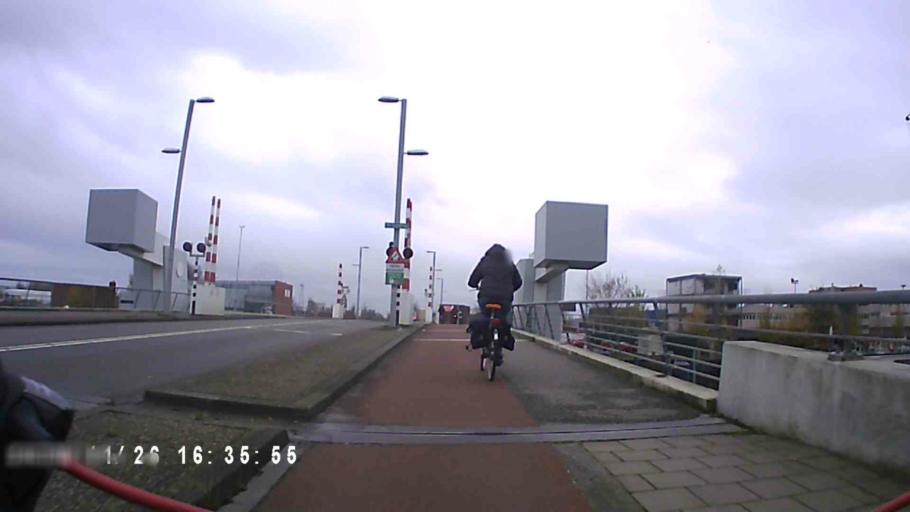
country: NL
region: Groningen
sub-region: Gemeente Groningen
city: Oosterpark
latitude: 53.2204
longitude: 6.5901
